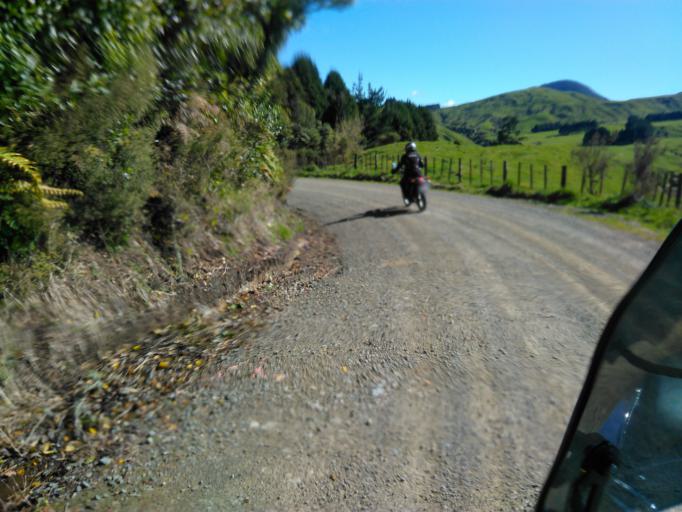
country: NZ
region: Bay of Plenty
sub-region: Opotiki District
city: Opotiki
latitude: -38.3488
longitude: 177.5850
